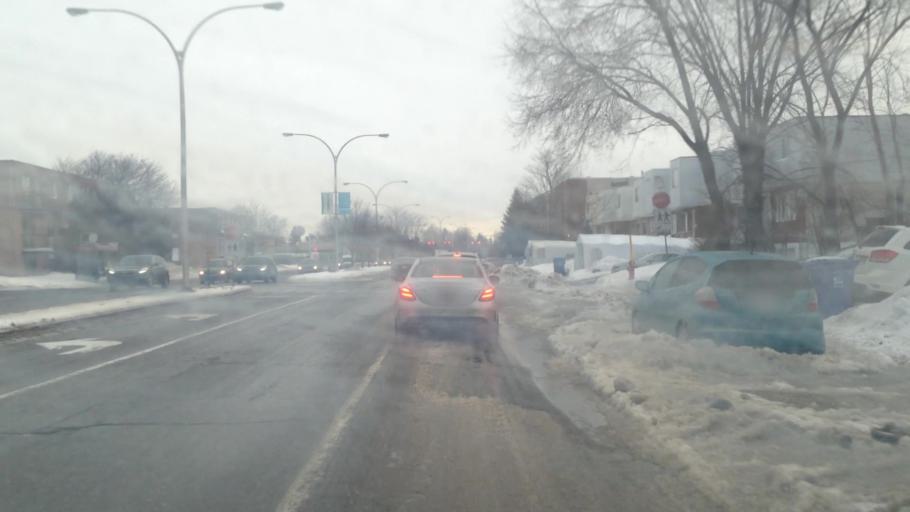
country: CA
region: Quebec
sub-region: Monteregie
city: Brossard
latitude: 45.4715
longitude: -73.4429
